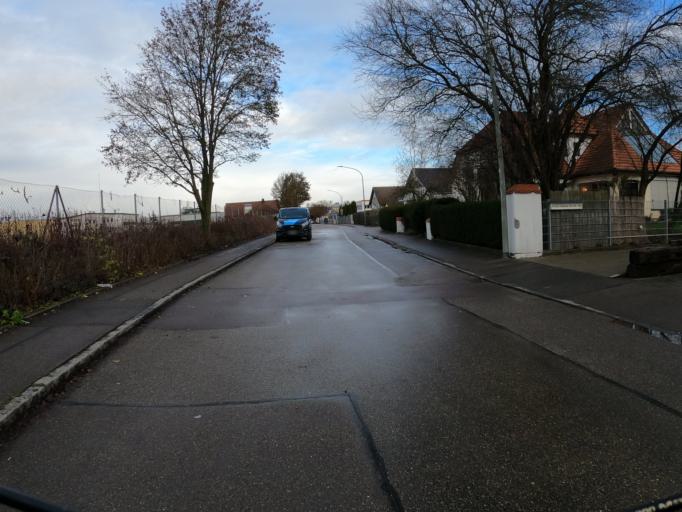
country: DE
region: Bavaria
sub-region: Swabia
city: Holzheim
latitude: 48.4207
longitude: 10.0669
